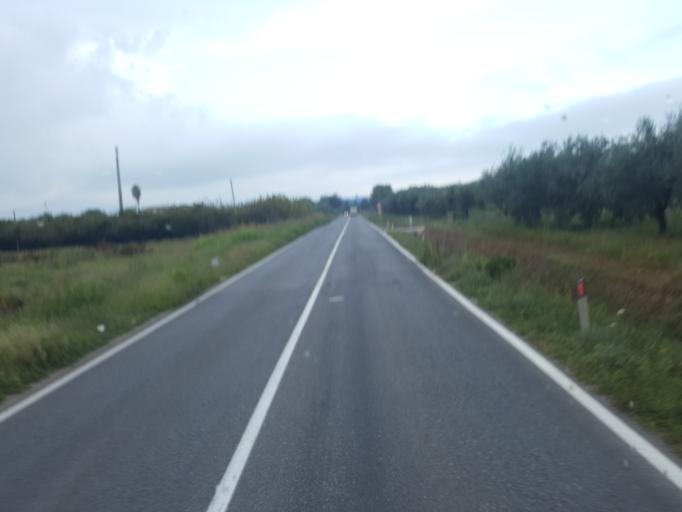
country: IT
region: Campania
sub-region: Provincia di Caserta
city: Sparanise
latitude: 41.1734
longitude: 14.1319
